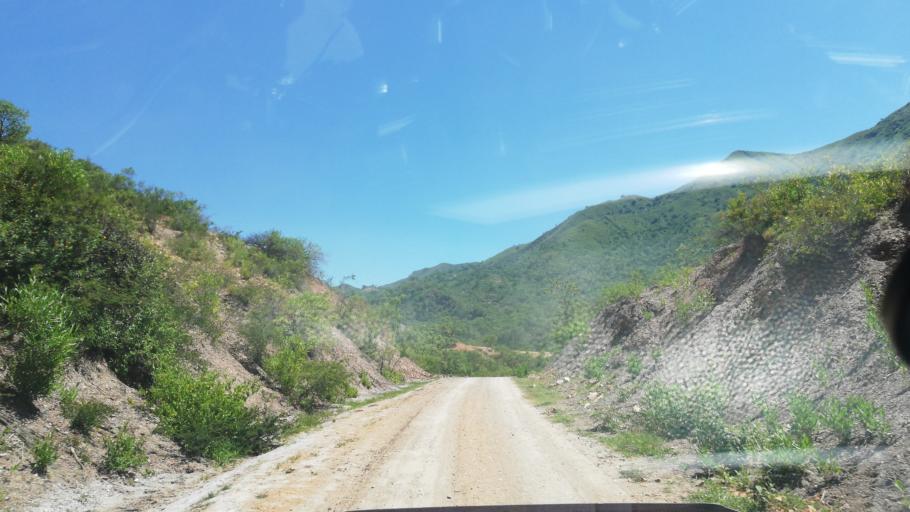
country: BO
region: Cochabamba
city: Mizque
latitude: -17.8839
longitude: -65.2859
